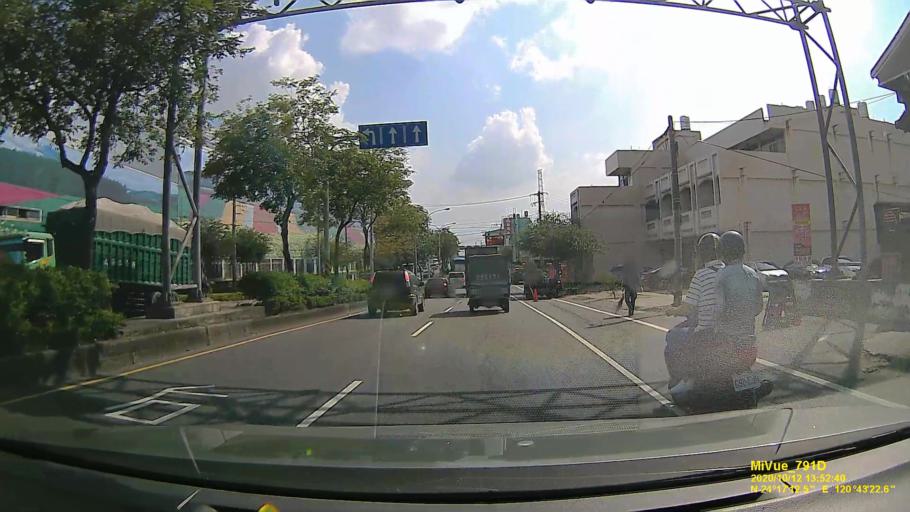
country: TW
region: Taiwan
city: Fengyuan
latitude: 24.2867
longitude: 120.7230
